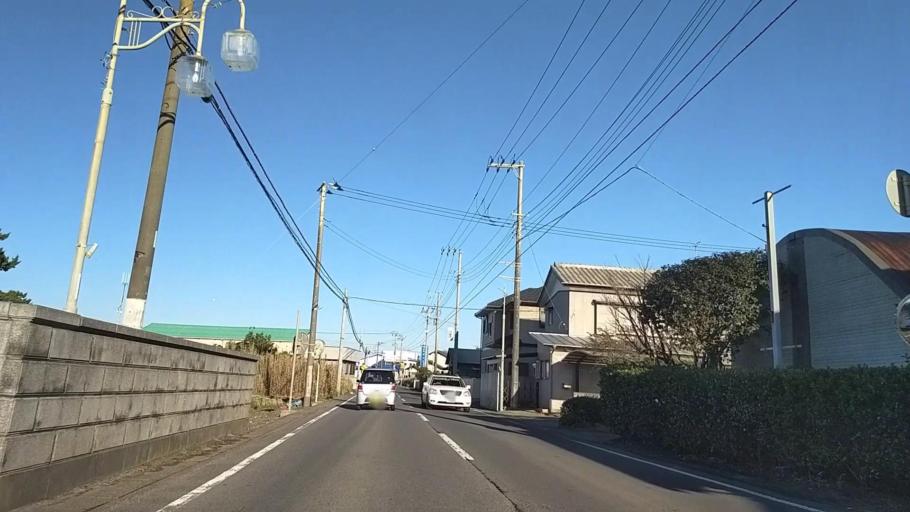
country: JP
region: Chiba
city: Asahi
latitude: 35.6921
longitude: 140.6600
